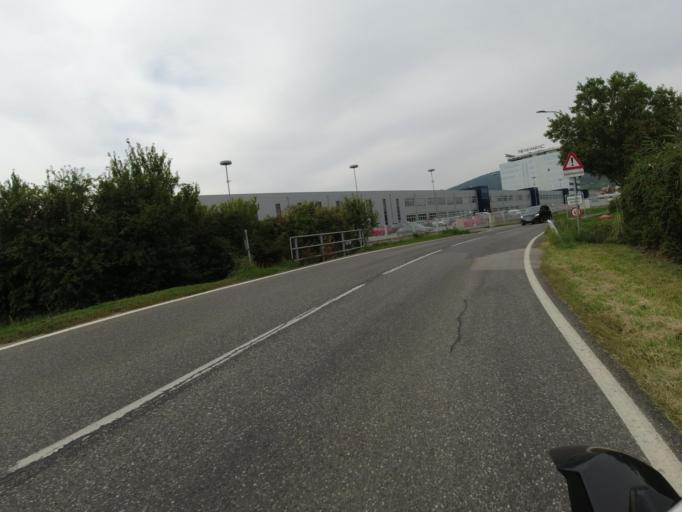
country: AT
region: Lower Austria
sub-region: Politischer Bezirk Baden
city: Traiskirchen
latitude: 48.0348
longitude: 16.2965
